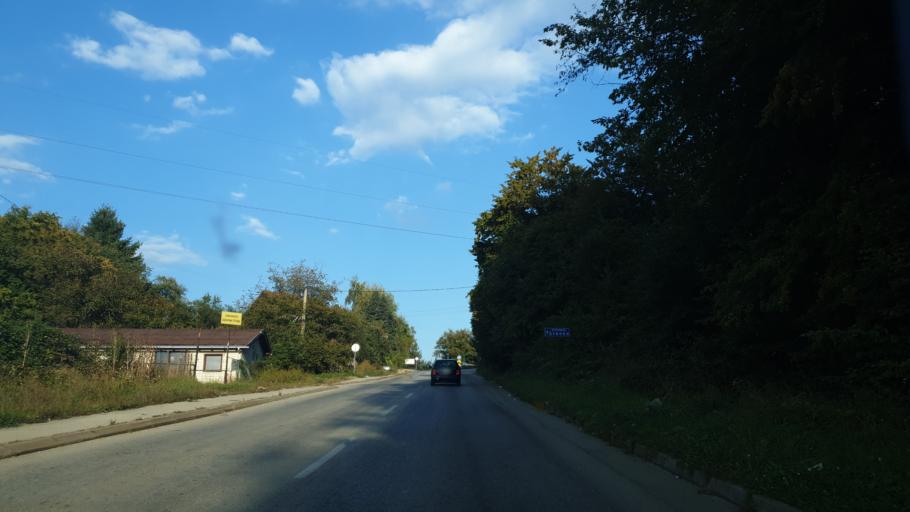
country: RS
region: Central Serbia
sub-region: Zlatiborski Okrug
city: Uzice
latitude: 43.8574
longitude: 19.8751
